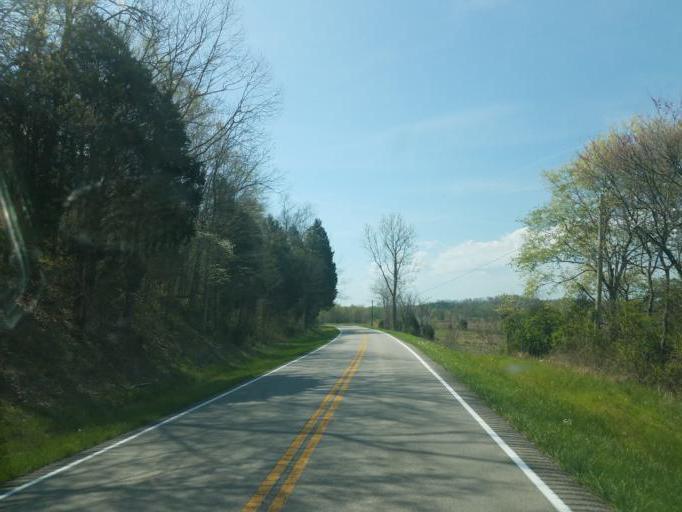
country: US
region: Kentucky
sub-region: Edmonson County
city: Brownsville
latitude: 37.2902
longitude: -86.4382
